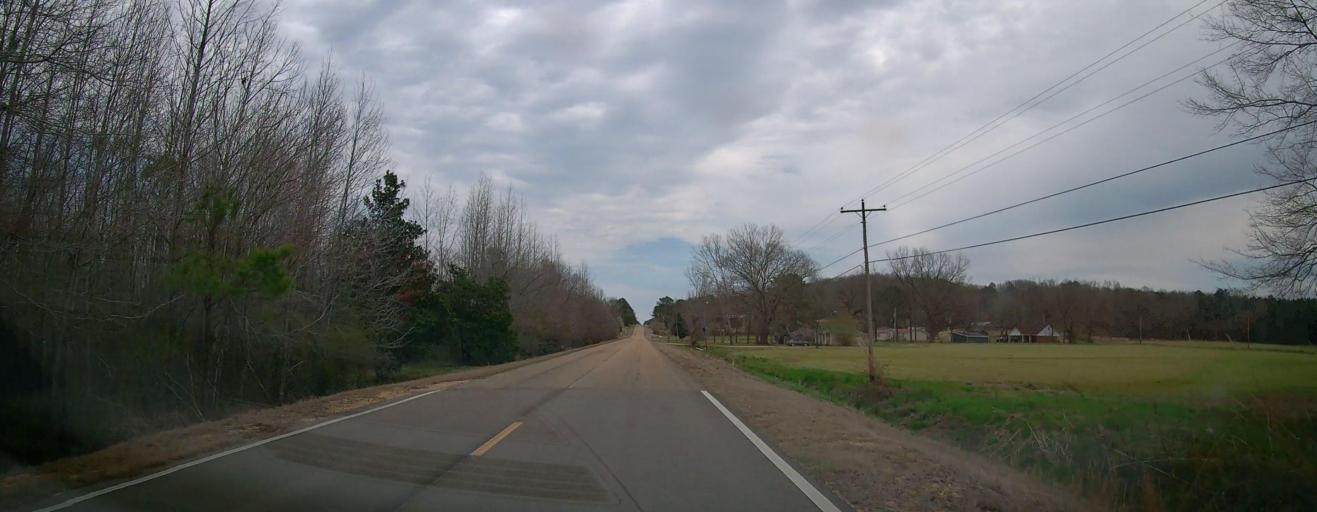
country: US
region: Mississippi
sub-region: Itawamba County
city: Fulton
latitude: 34.2251
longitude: -88.2273
